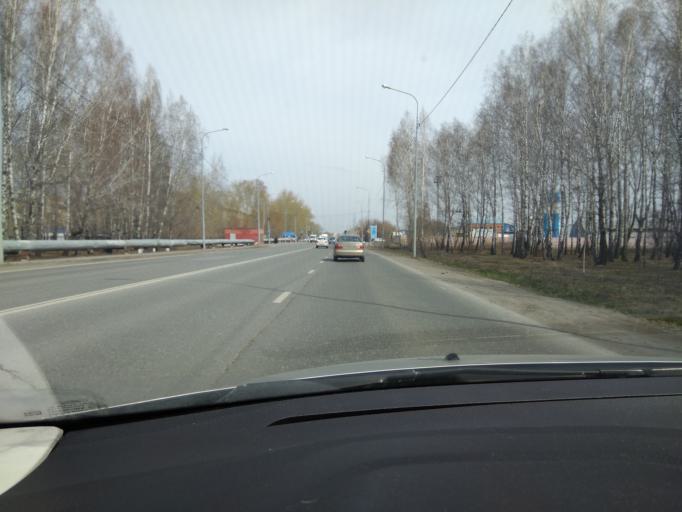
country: RU
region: Tjumen
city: Melioratorov
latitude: 57.1817
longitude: 65.5918
